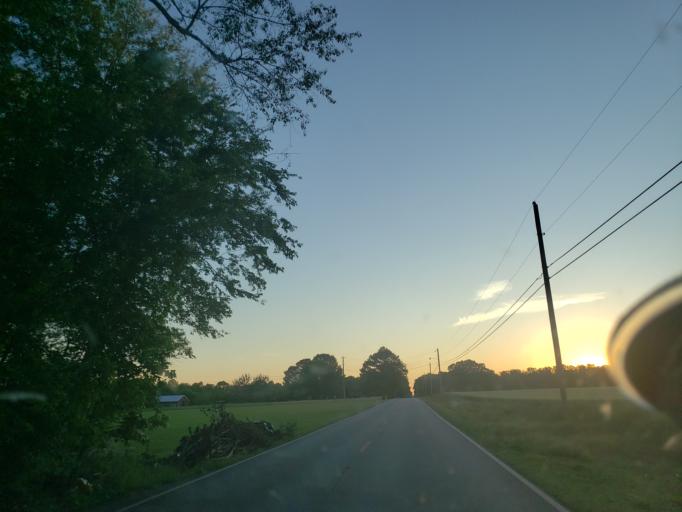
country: US
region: Alabama
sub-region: Madison County
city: Hazel Green
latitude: 34.9769
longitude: -86.6238
